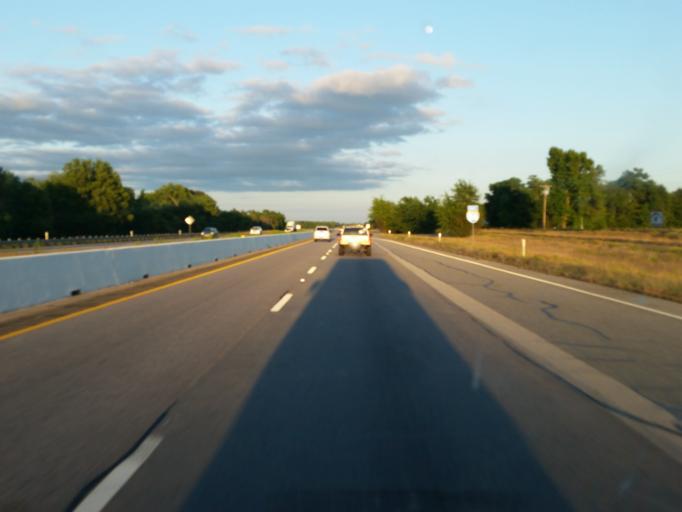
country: US
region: Texas
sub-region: Van Zandt County
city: Canton
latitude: 32.5405
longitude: -95.7518
